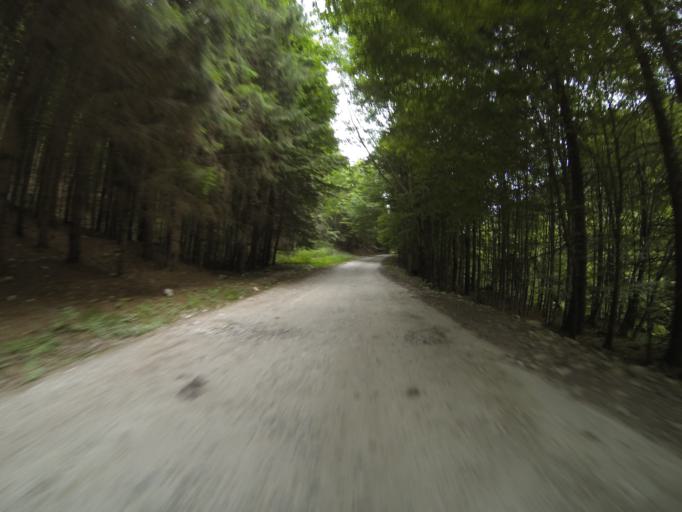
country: RO
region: Gorj
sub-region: Comuna Polovragi
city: Polovragi
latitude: 45.2333
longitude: 23.7711
